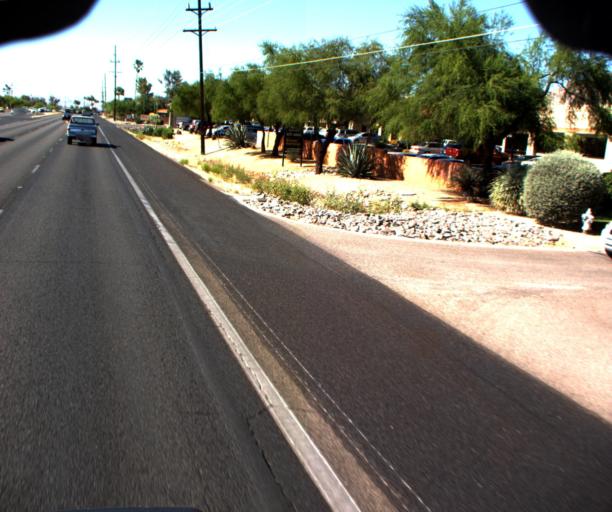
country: US
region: Arizona
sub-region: Pima County
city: Casas Adobes
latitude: 32.3289
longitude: -110.9761
